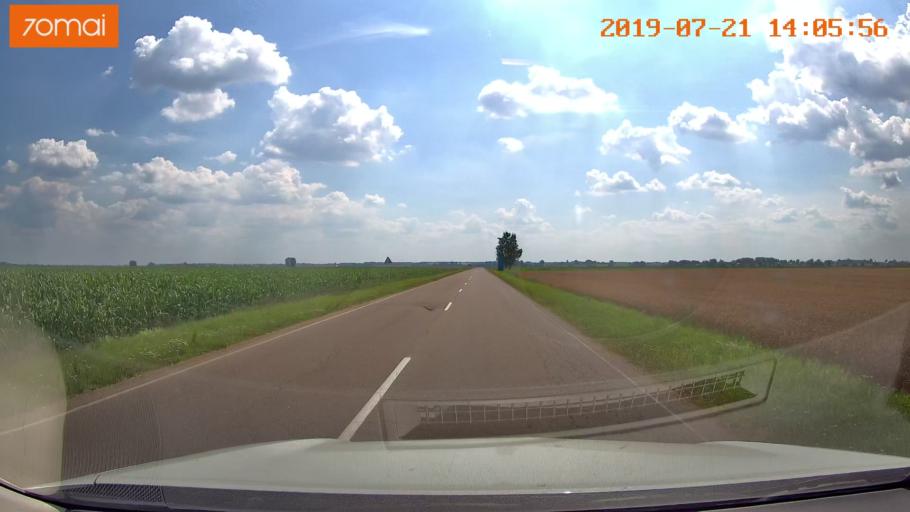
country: BY
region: Grodnenskaya
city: Lyubcha
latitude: 53.7045
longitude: 26.1119
